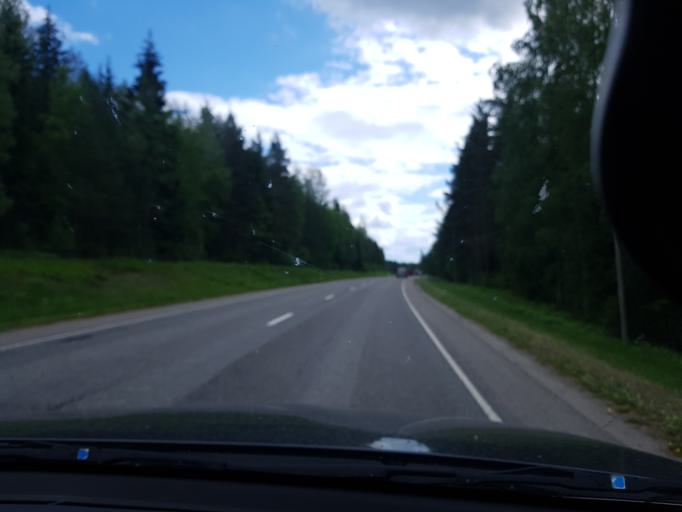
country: FI
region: Pirkanmaa
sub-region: Tampere
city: Paelkaene
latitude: 61.3063
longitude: 24.2971
